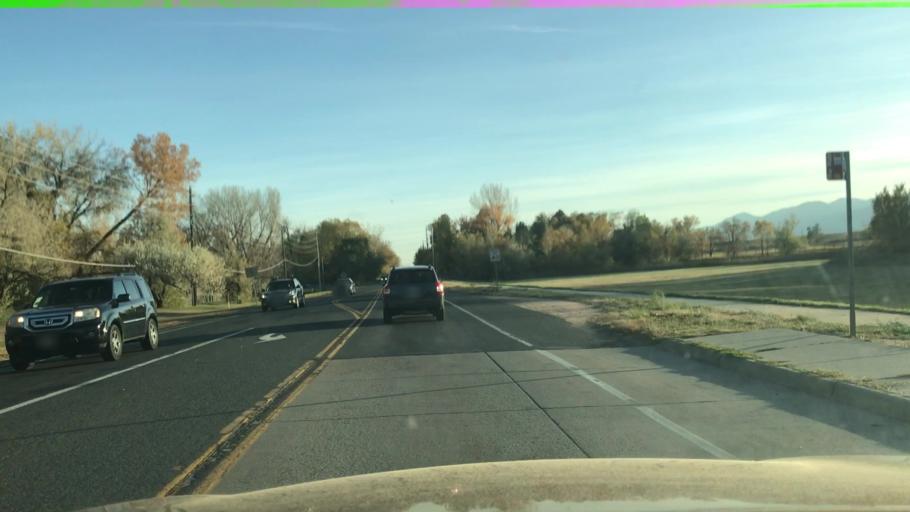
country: US
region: Colorado
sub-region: Boulder County
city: Gunbarrel
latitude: 40.0564
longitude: -105.2068
